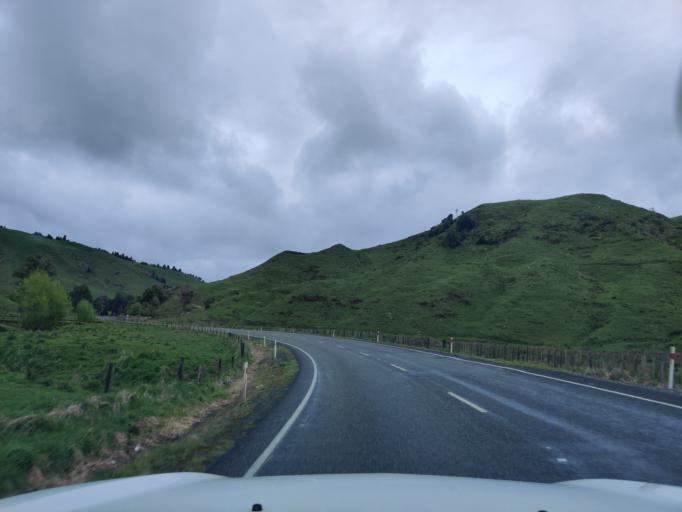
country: NZ
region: Waikato
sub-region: Otorohanga District
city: Otorohanga
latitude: -38.5512
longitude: 175.1949
